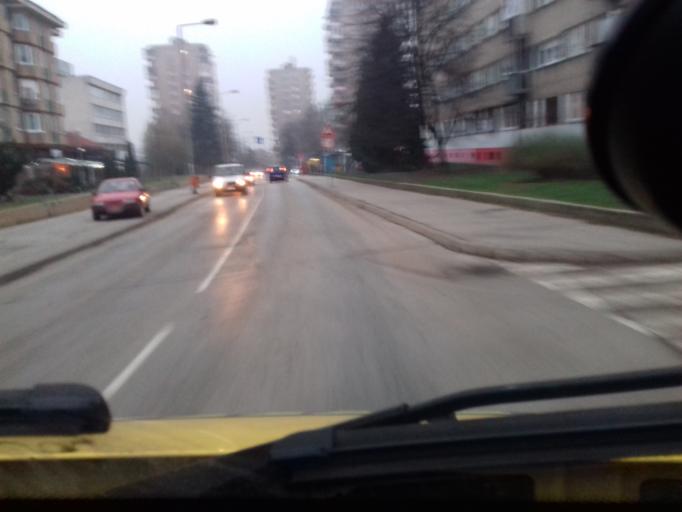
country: BA
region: Federation of Bosnia and Herzegovina
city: Zenica
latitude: 44.2060
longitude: 17.9230
